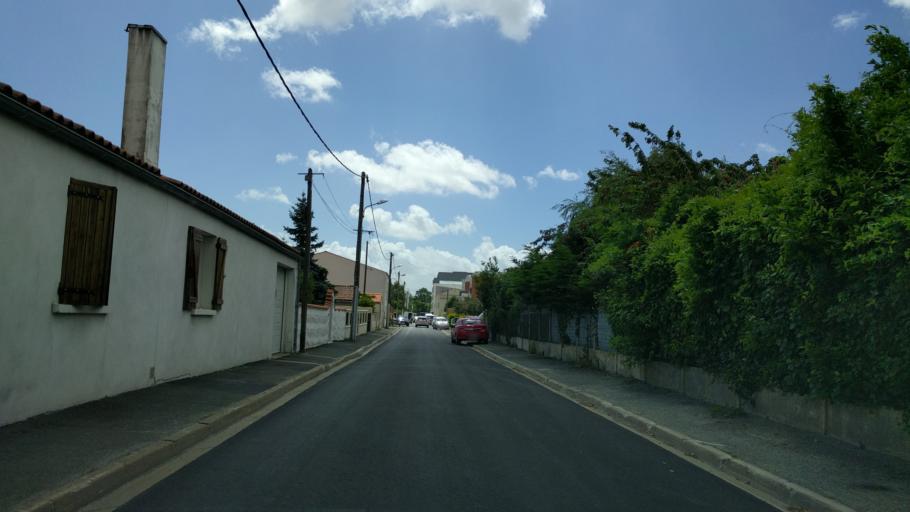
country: FR
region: Poitou-Charentes
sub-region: Departement de la Charente-Maritime
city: La Rochelle
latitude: 46.1610
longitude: -1.1353
